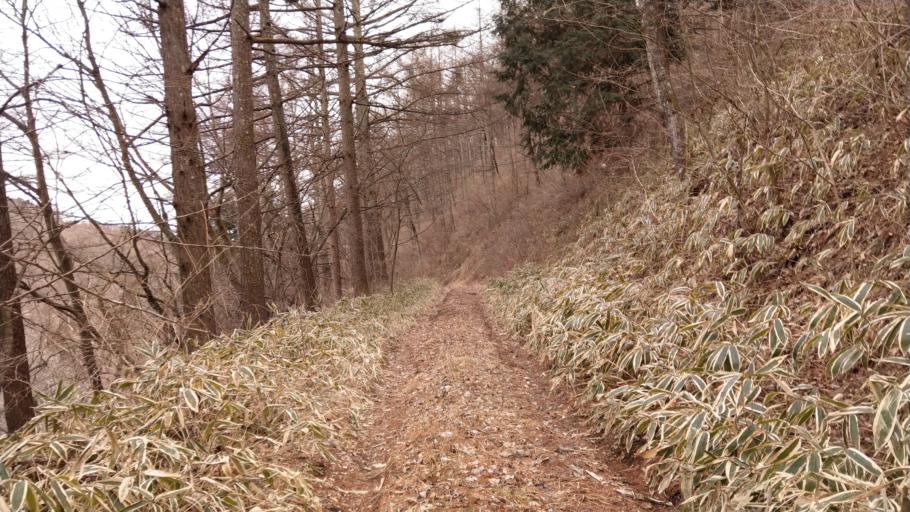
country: JP
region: Nagano
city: Komoro
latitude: 36.3690
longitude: 138.4411
